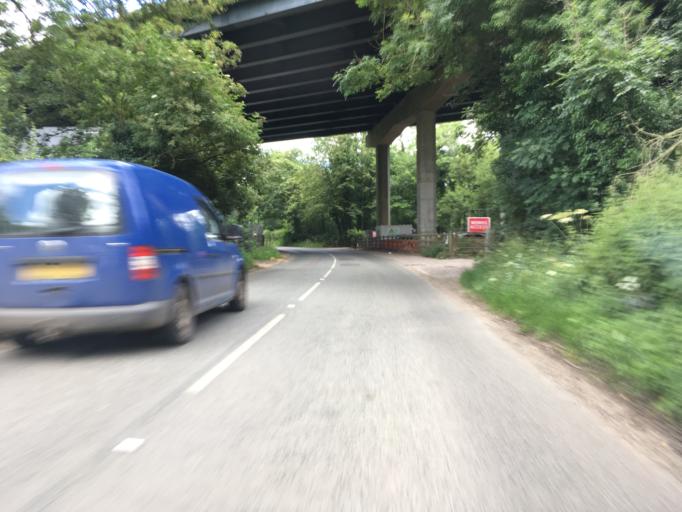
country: GB
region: England
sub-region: West Berkshire
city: Welford
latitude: 51.4503
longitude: -1.4050
